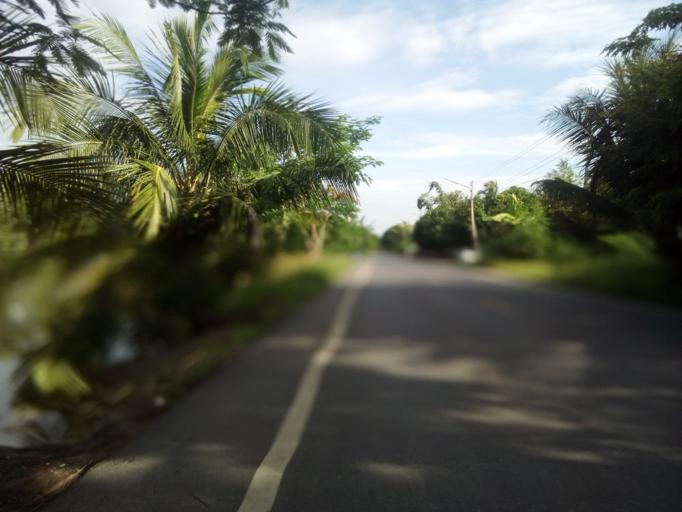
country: TH
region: Pathum Thani
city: Nong Suea
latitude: 14.0993
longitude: 100.8461
